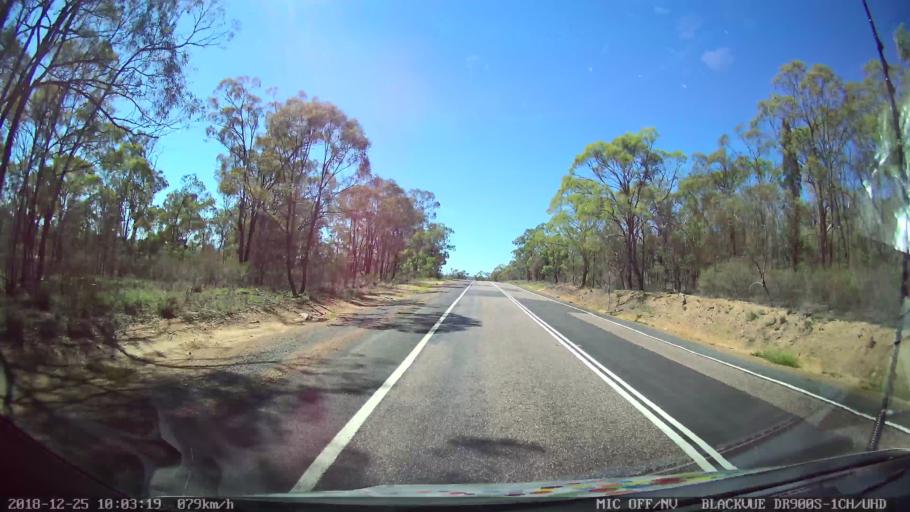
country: AU
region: New South Wales
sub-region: Upper Hunter Shire
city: Merriwa
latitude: -32.2274
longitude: 150.4701
